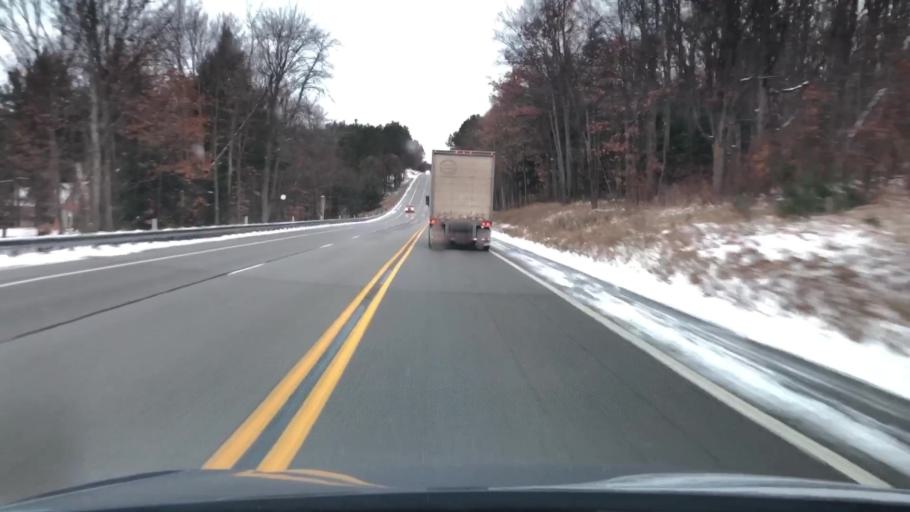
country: US
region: Michigan
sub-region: Wexford County
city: Cadillac
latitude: 44.1834
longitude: -85.3852
